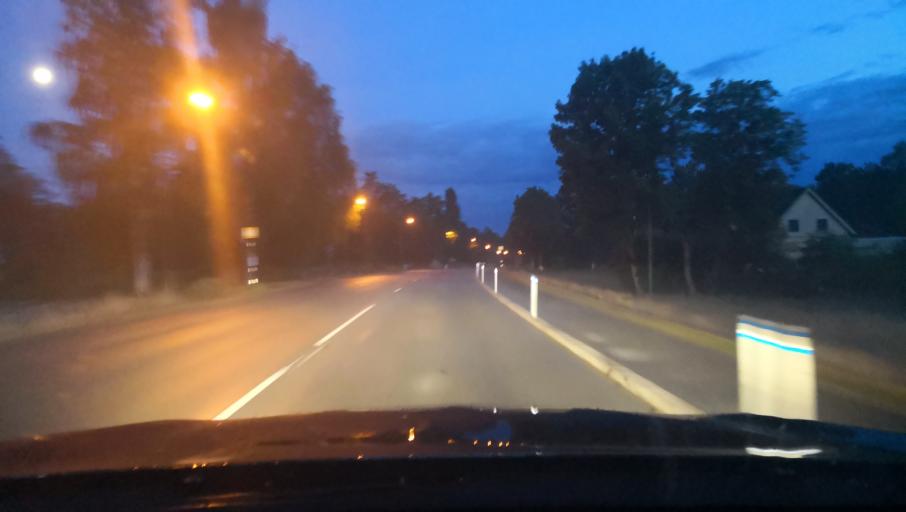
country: SE
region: Skane
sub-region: Osby Kommun
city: Osby
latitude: 56.3624
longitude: 13.9799
